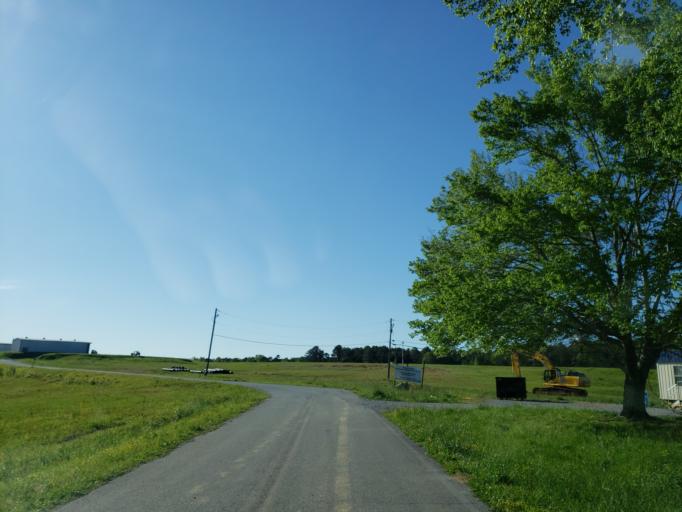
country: US
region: Georgia
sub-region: Polk County
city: Aragon
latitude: 34.0172
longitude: -85.1467
